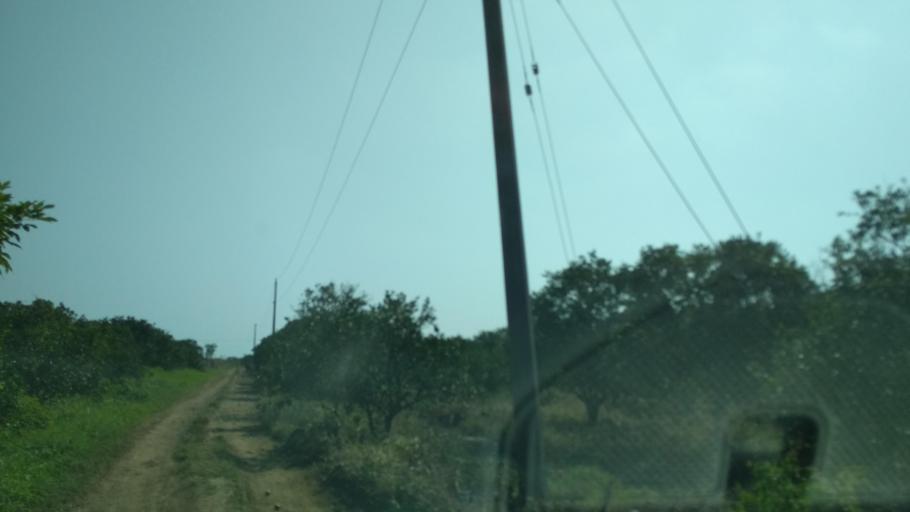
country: MX
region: Puebla
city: San Jose Acateno
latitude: 20.2041
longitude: -97.1817
